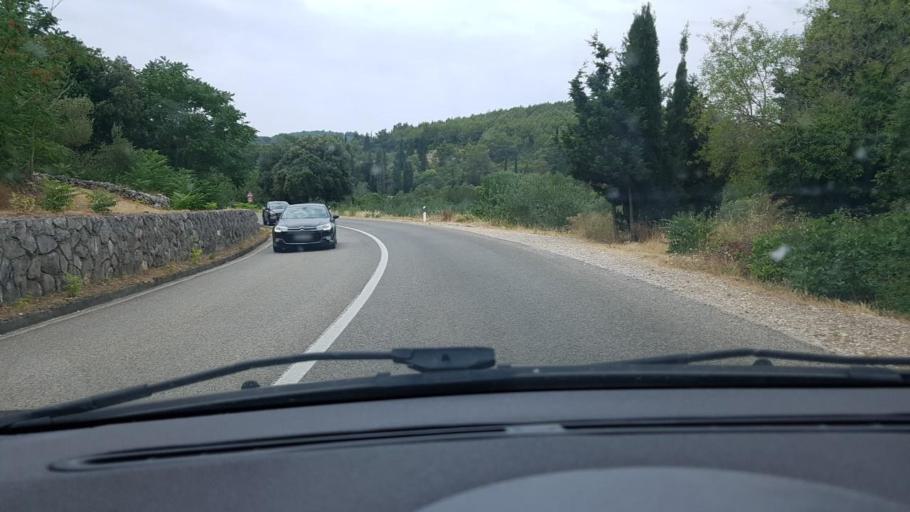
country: HR
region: Dubrovacko-Neretvanska
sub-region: Grad Korcula
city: Zrnovo
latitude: 42.9436
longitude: 17.1056
